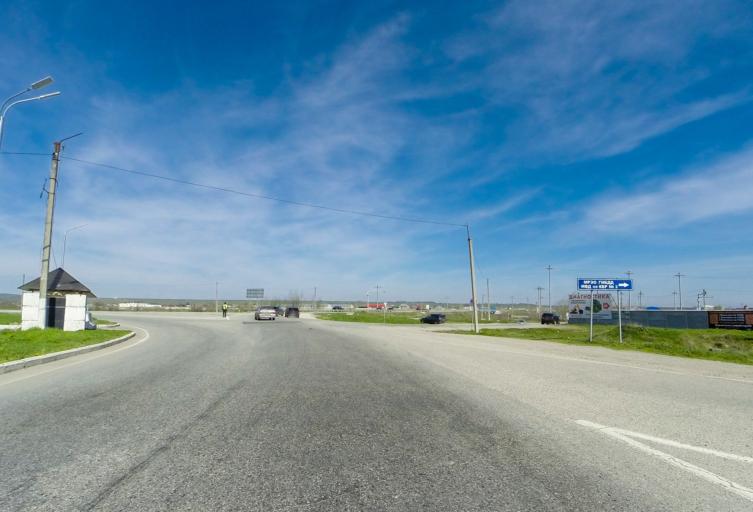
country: RU
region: Kabardino-Balkariya
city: Islamey
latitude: 43.6697
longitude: 43.4958
